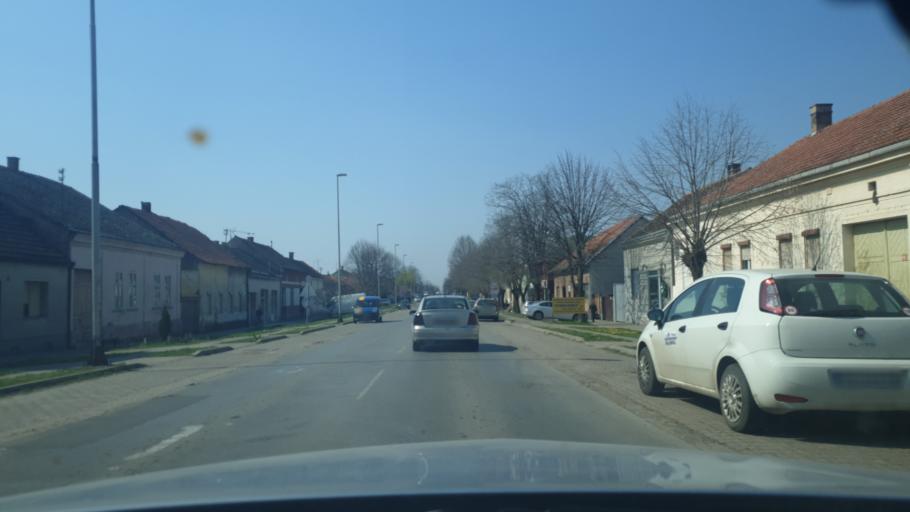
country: RS
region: Autonomna Pokrajina Vojvodina
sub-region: Sremski Okrug
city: Ruma
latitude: 45.0081
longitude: 19.8103
